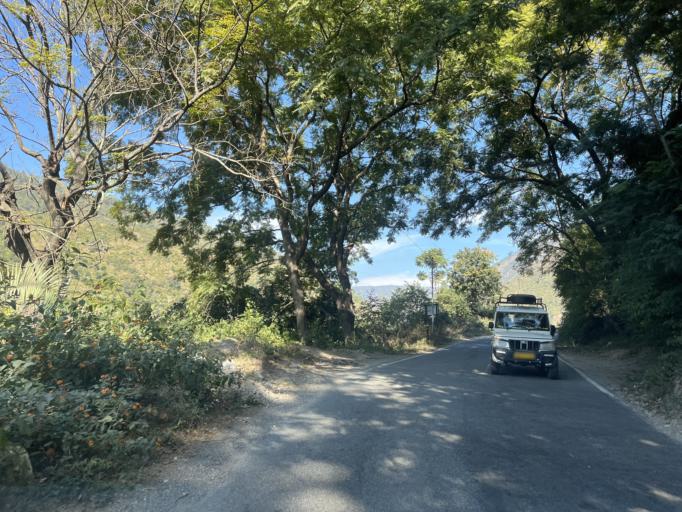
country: IN
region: Uttarakhand
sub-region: Naini Tal
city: Naini Tal
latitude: 29.5221
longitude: 79.4819
